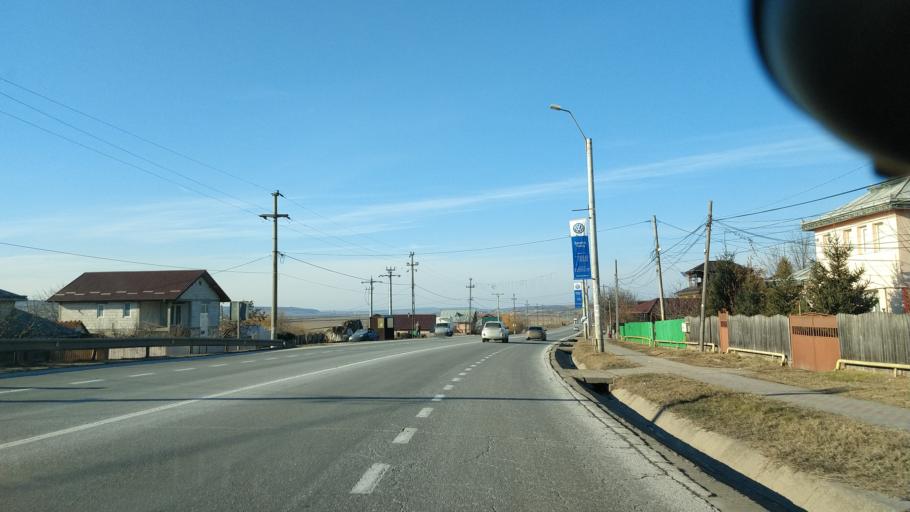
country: RO
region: Iasi
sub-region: Comuna Letcani
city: Letcani
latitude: 47.1959
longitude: 27.3987
